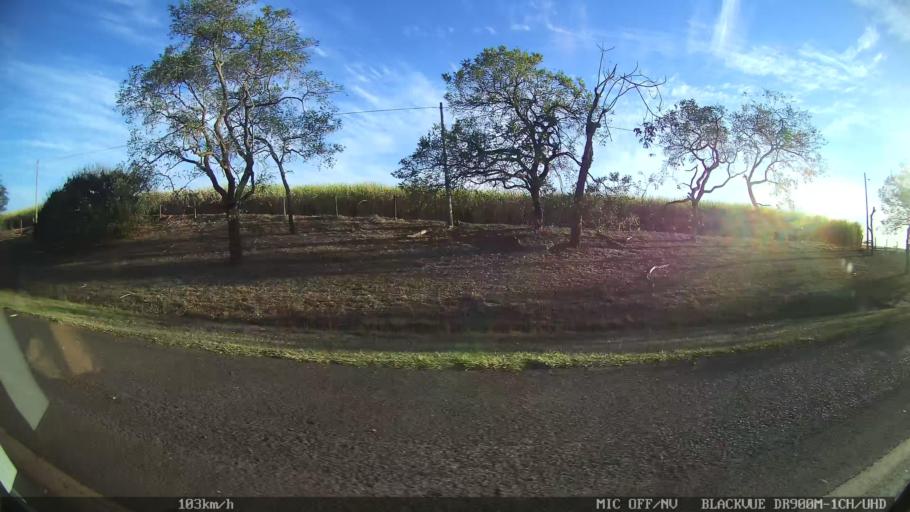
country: BR
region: Sao Paulo
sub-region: Urupes
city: Urupes
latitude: -21.0127
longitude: -49.1777
